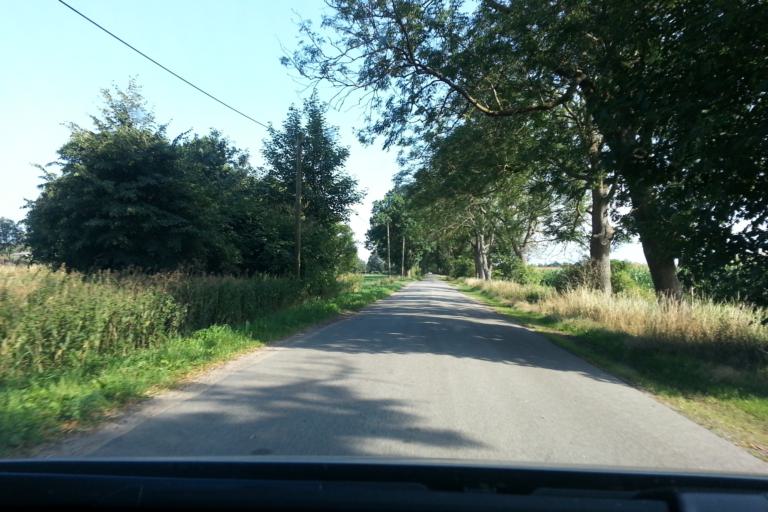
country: DE
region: Mecklenburg-Vorpommern
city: Ferdinandshof
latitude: 53.6434
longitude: 13.8127
